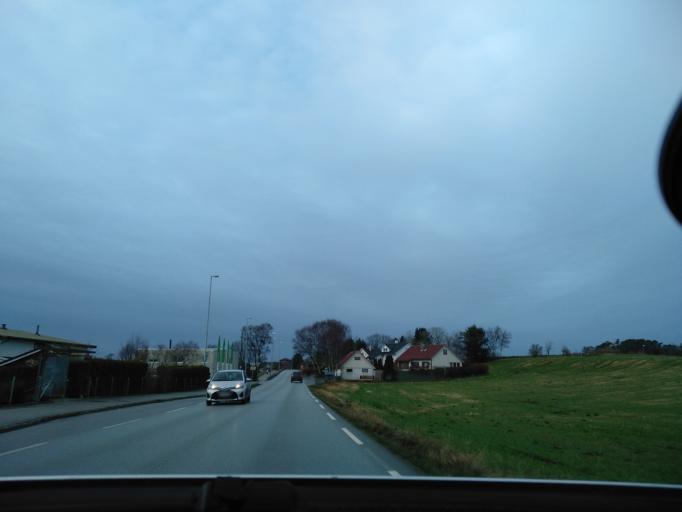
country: NO
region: Rogaland
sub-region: Randaberg
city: Randaberg
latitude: 58.9966
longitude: 5.6300
